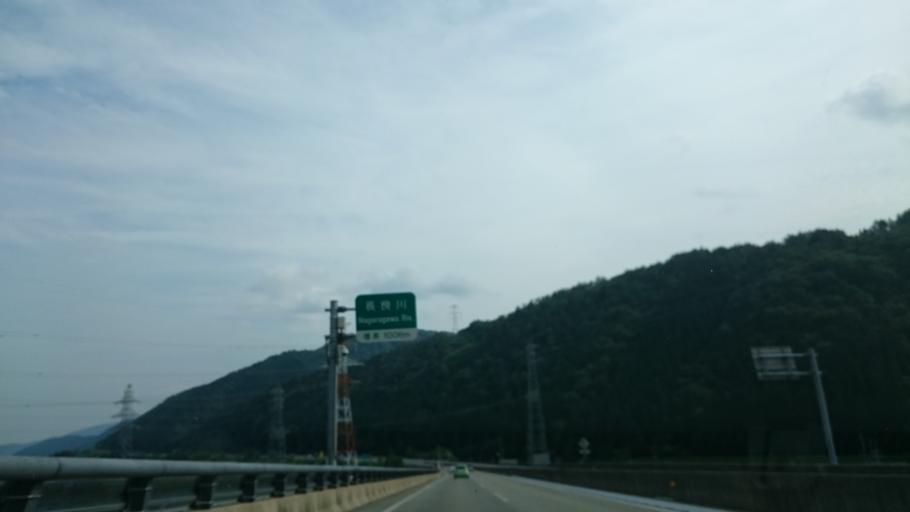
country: JP
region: Gifu
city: Gujo
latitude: 35.8510
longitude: 136.8723
